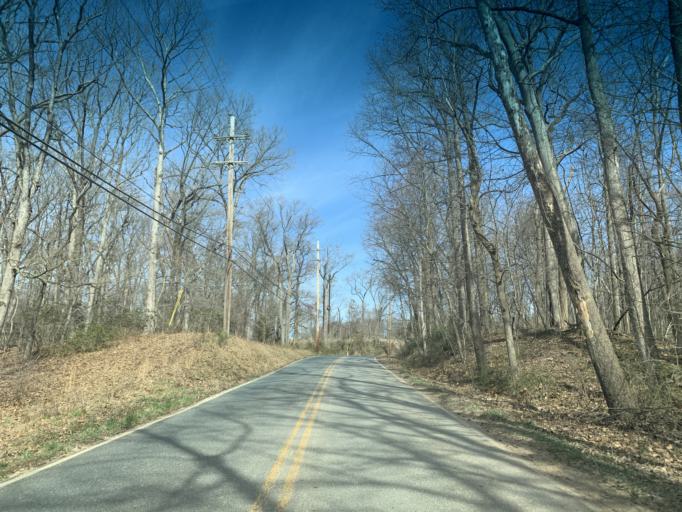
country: US
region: Maryland
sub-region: Cecil County
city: Charlestown
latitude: 39.5711
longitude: -76.0231
